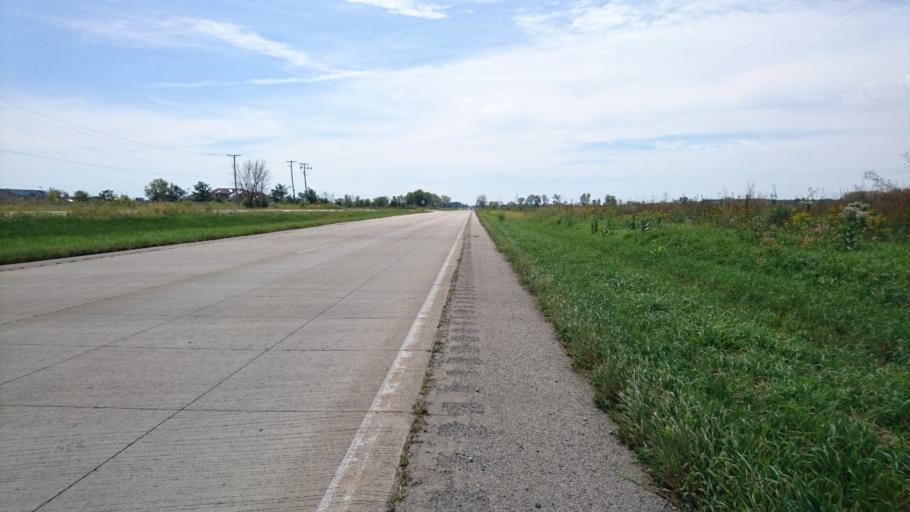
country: US
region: Illinois
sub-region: Will County
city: Wilmington
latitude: 41.3448
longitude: -88.1335
